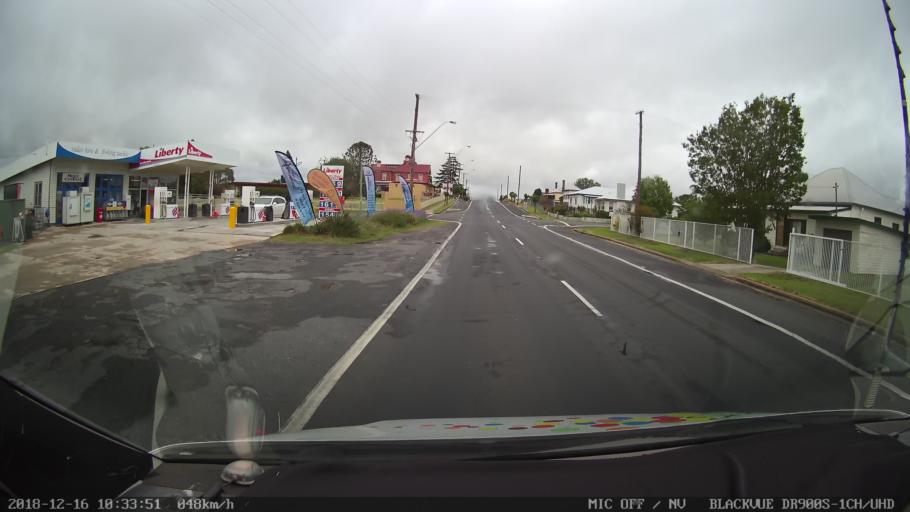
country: AU
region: New South Wales
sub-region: Tenterfield Municipality
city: Carrolls Creek
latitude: -29.0619
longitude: 152.0176
